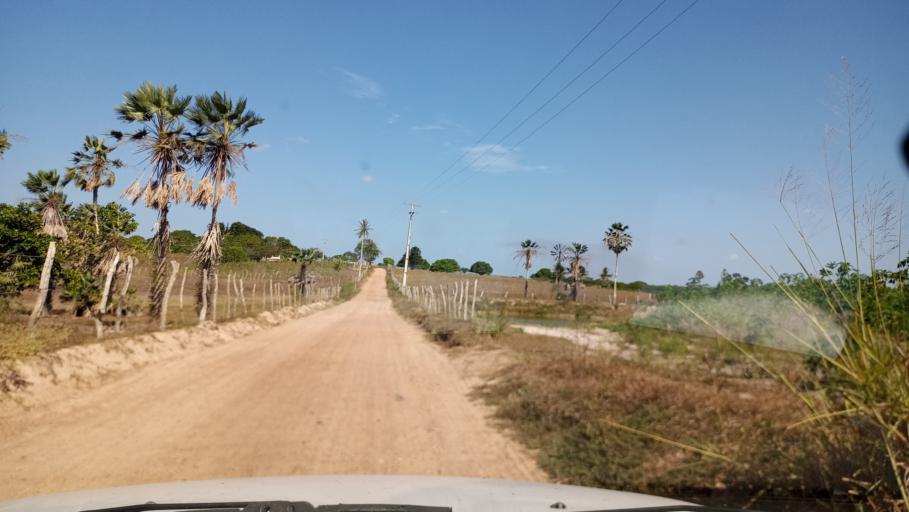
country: BR
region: Rio Grande do Norte
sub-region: Brejinho
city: Brejinho
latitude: -6.1759
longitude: -35.4600
